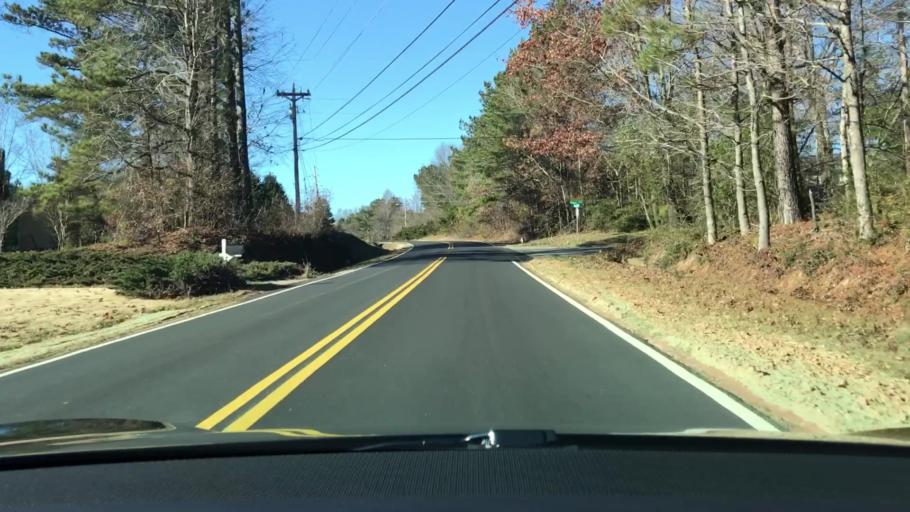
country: US
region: Georgia
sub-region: Barrow County
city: Auburn
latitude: 34.0804
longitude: -83.8659
